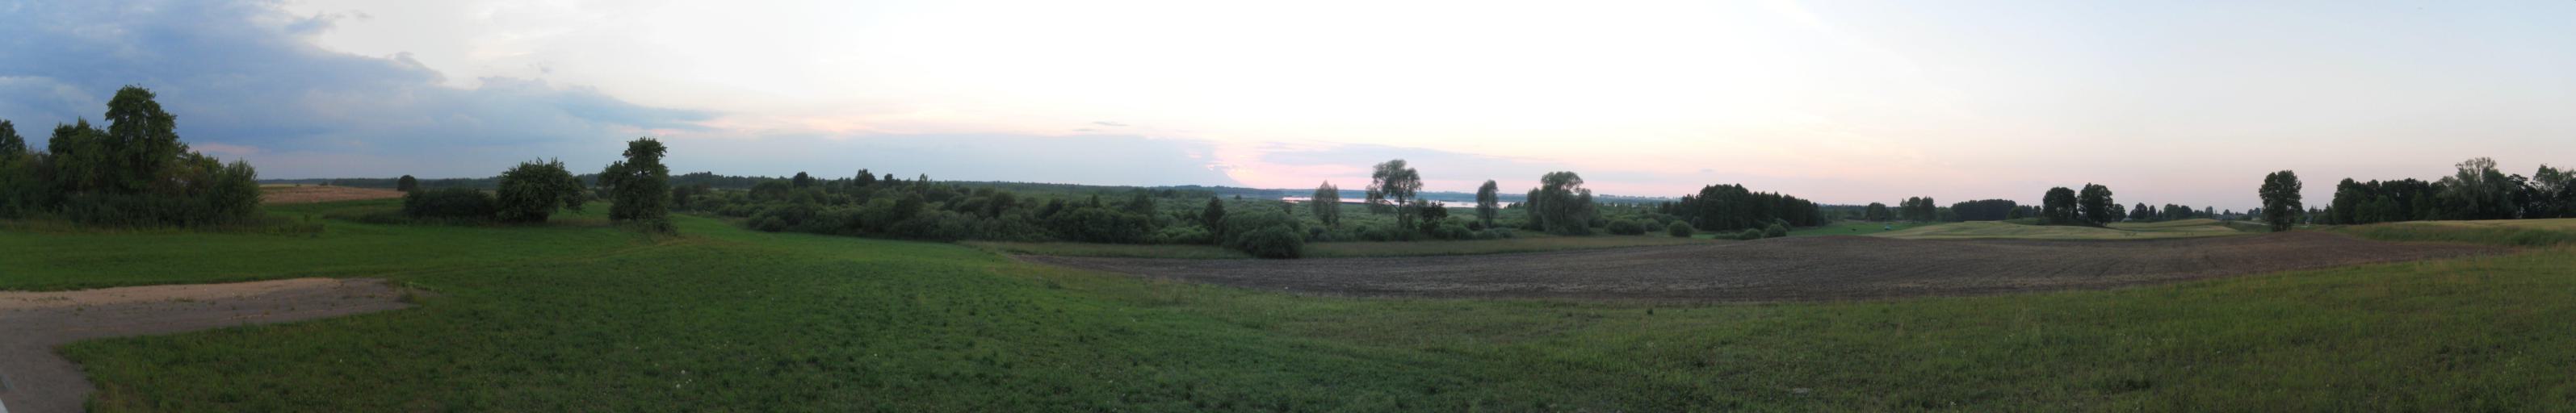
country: LT
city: Simnas
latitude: 54.4845
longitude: 23.6779
